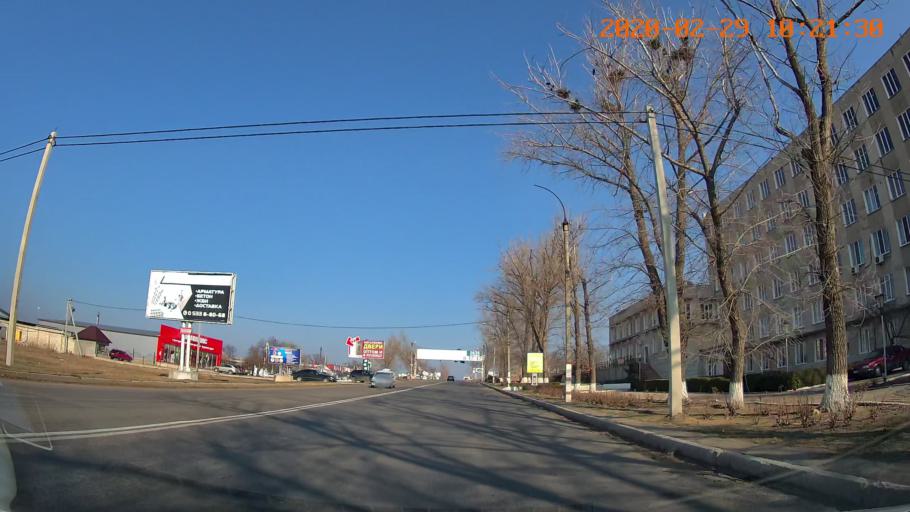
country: MD
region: Telenesti
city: Tiraspolul Nou
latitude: 46.8671
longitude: 29.6092
